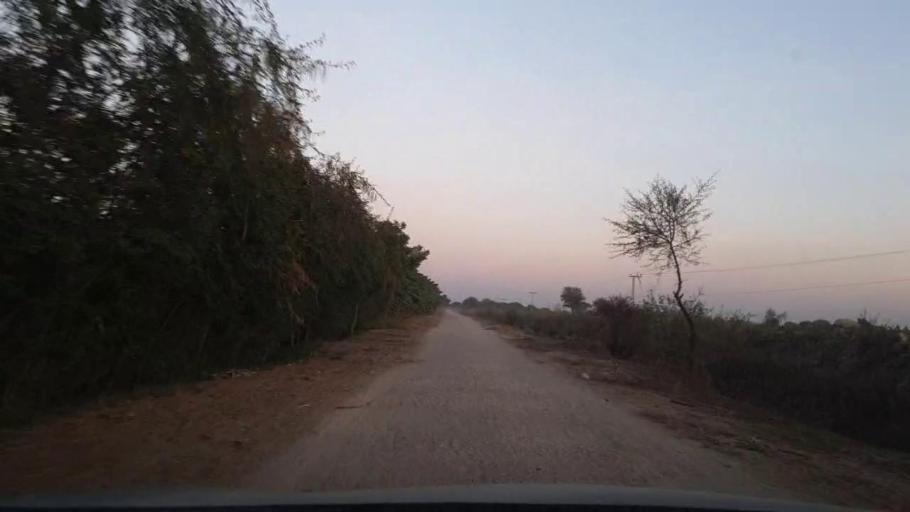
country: PK
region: Sindh
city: Tando Allahyar
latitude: 25.5576
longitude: 68.7807
